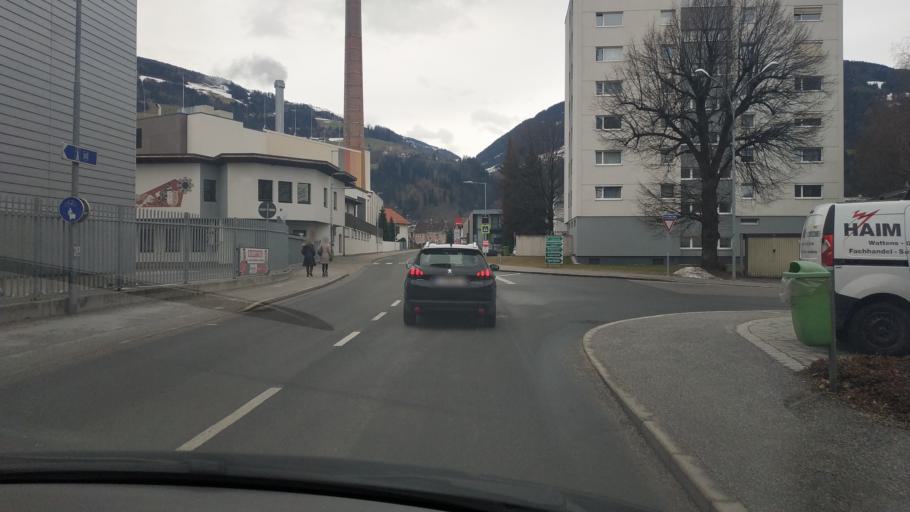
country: AT
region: Tyrol
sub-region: Politischer Bezirk Innsbruck Land
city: Fritzens
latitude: 47.2950
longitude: 11.5891
